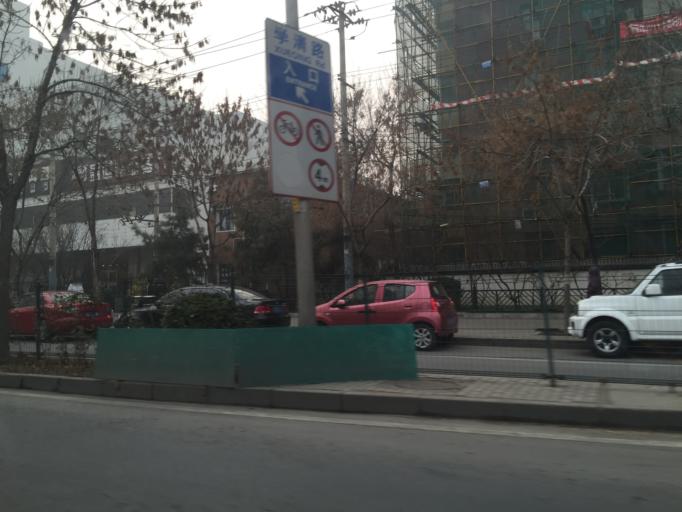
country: CN
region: Beijing
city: Qinghe
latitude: 40.0012
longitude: 116.3463
